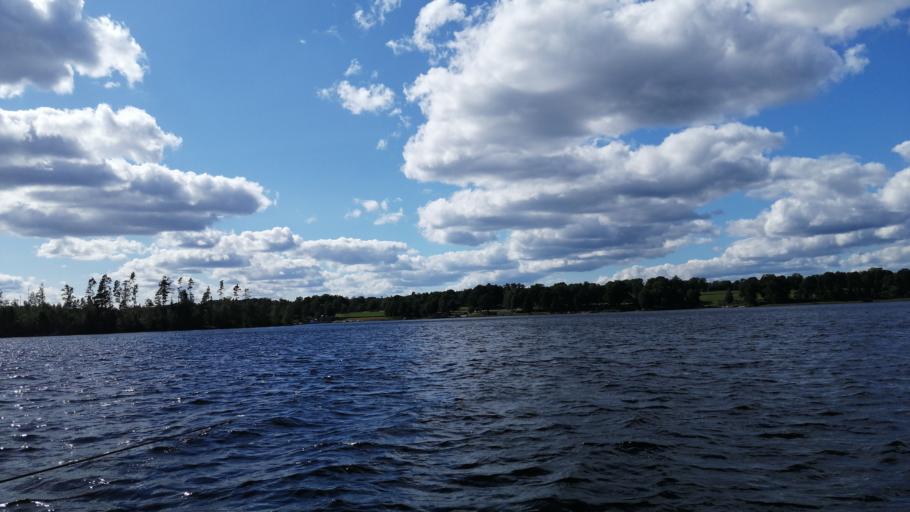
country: SE
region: Joenkoeping
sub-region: Varnamo Kommun
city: Bredaryd
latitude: 57.0078
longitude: 13.7112
